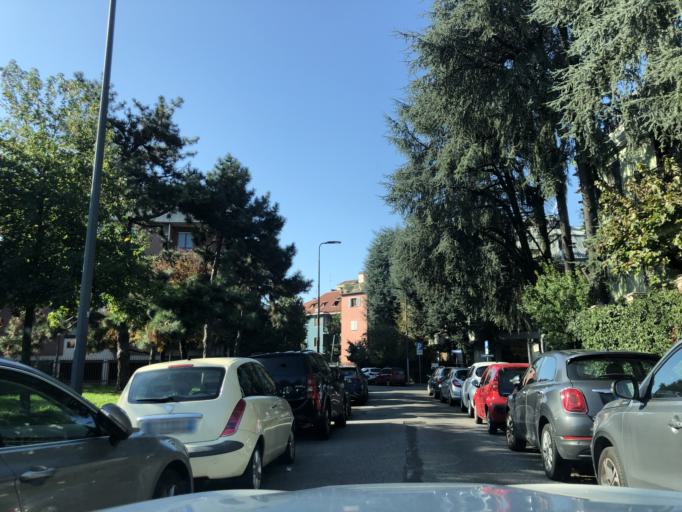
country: IT
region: Lombardy
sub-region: Citta metropolitana di Milano
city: Milano
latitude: 45.4983
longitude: 9.1994
